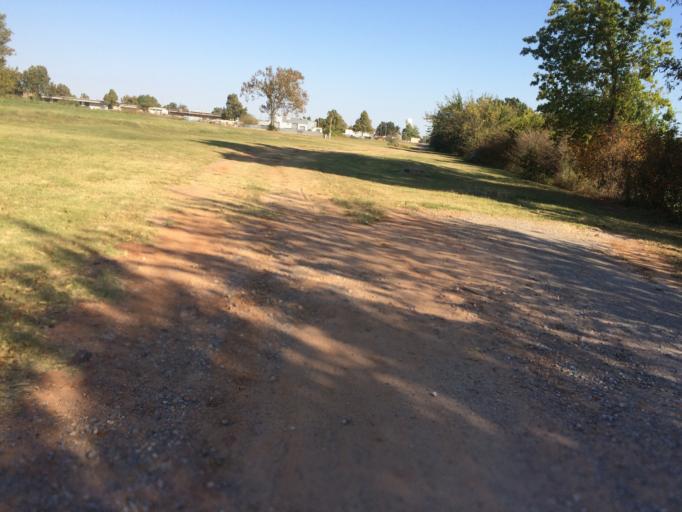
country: US
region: Oklahoma
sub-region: Cleveland County
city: Norman
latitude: 35.1821
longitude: -97.4323
